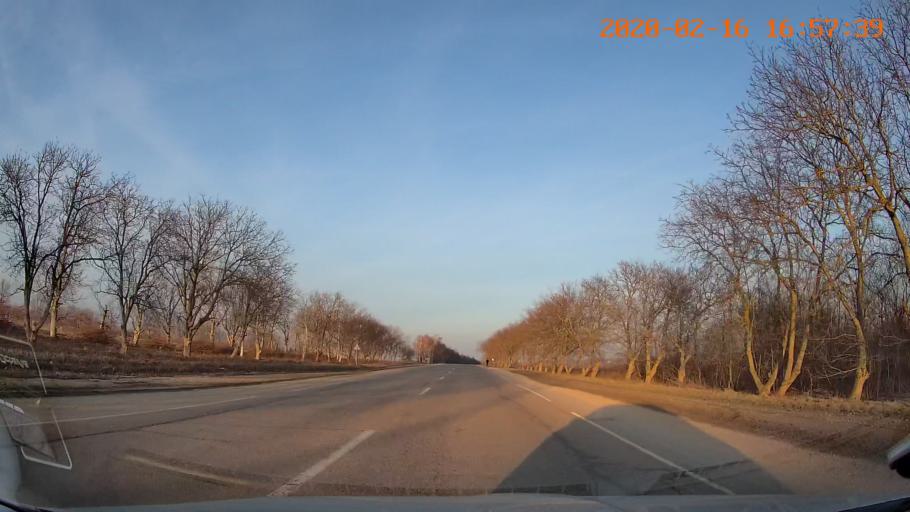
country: MD
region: Briceni
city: Briceni
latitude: 48.3445
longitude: 27.0711
